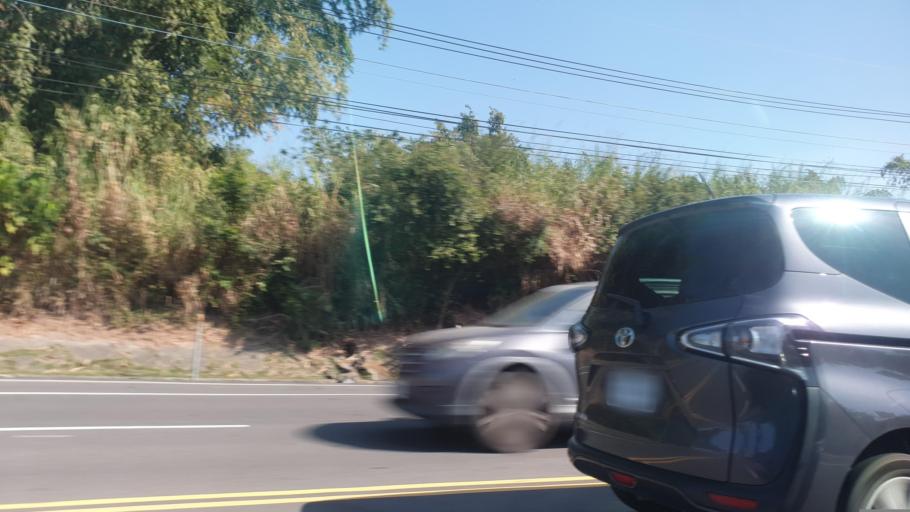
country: TW
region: Taiwan
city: Yujing
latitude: 23.0616
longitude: 120.3904
